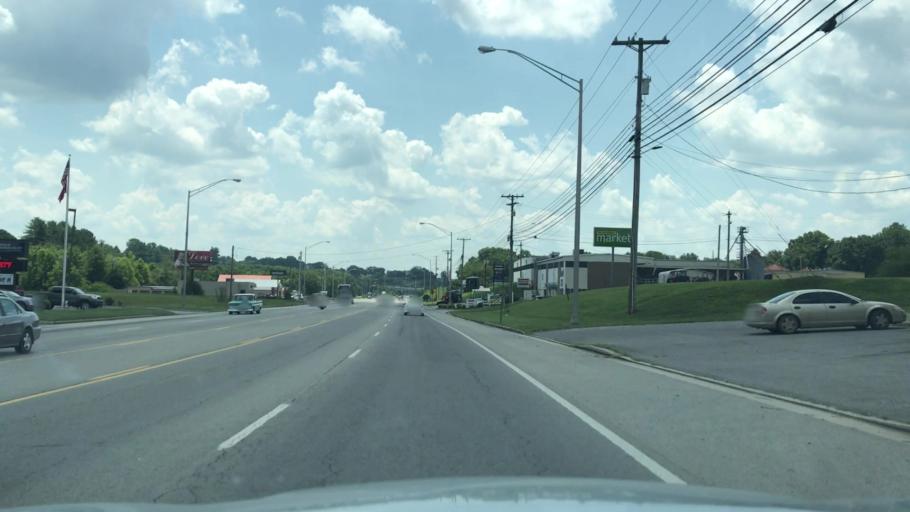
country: US
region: Tennessee
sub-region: Overton County
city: Livingston
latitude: 36.3709
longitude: -85.3410
